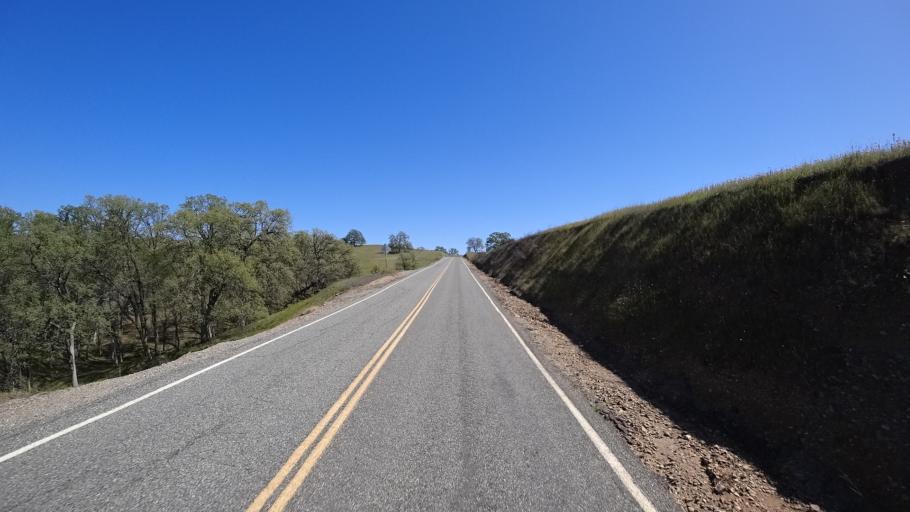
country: US
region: California
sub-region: Tehama County
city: Rancho Tehama Reserve
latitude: 39.8111
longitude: -122.4051
